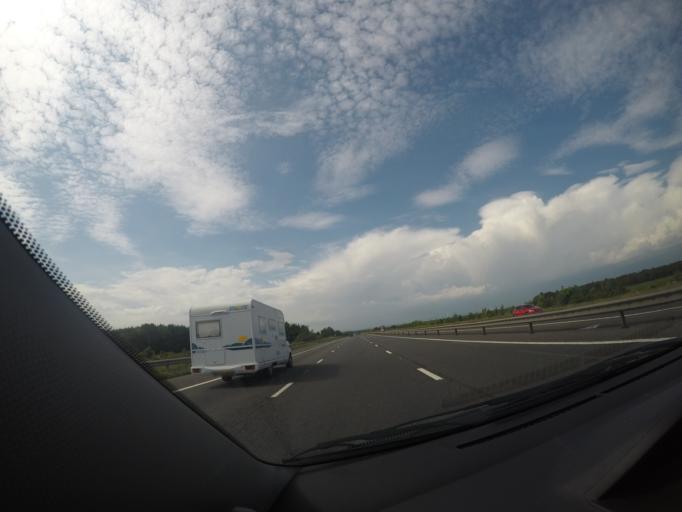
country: GB
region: Scotland
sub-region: Dumfries and Galloway
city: Gretna
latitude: 54.9694
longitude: -3.0029
